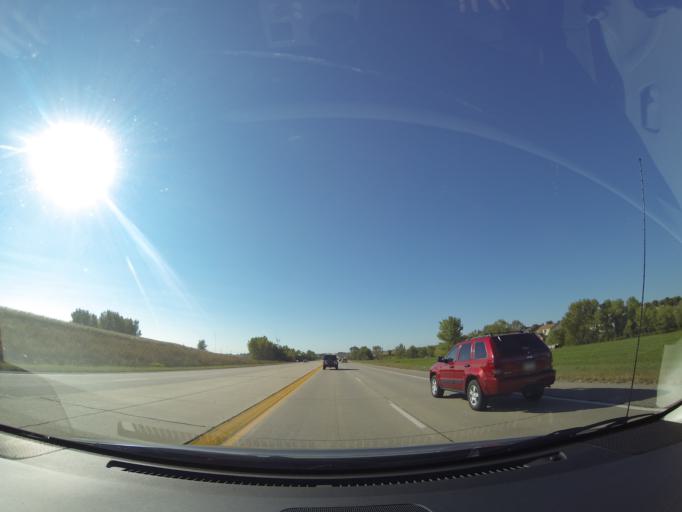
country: US
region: Nebraska
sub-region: Sarpy County
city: Gretna
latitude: 41.1229
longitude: -96.2533
